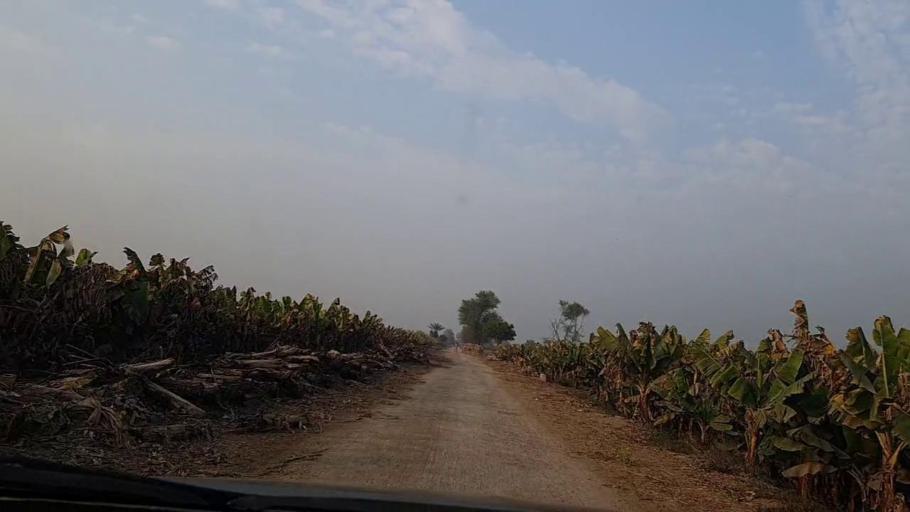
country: PK
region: Sindh
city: Nawabshah
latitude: 26.2898
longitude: 68.2854
